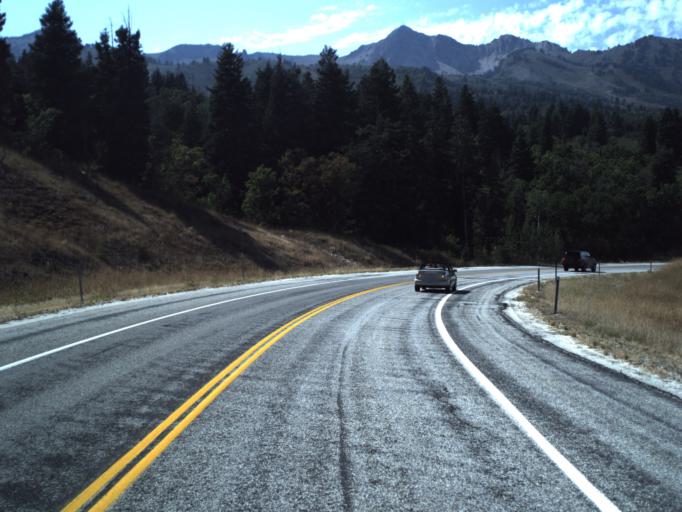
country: US
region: Utah
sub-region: Morgan County
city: Mountain Green
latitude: 41.2039
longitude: -111.8327
